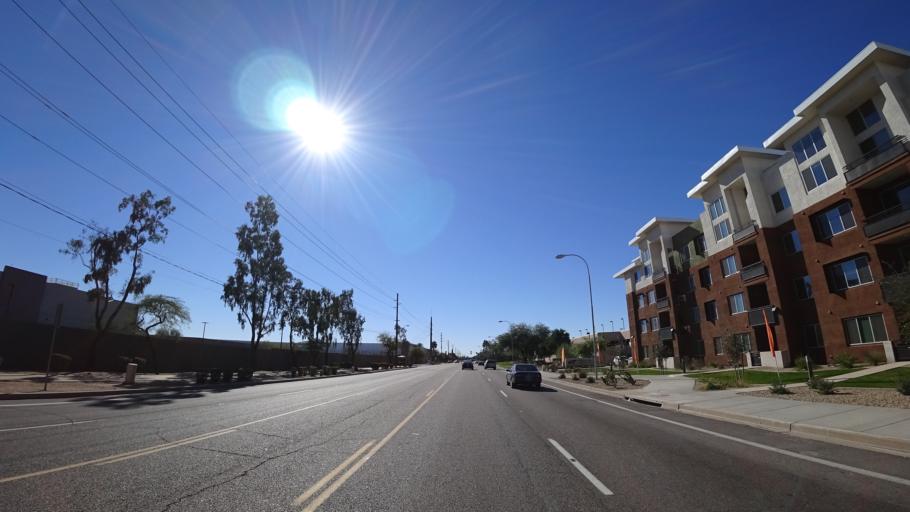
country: US
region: Arizona
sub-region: Maricopa County
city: Tempe Junction
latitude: 33.4020
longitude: -111.9608
